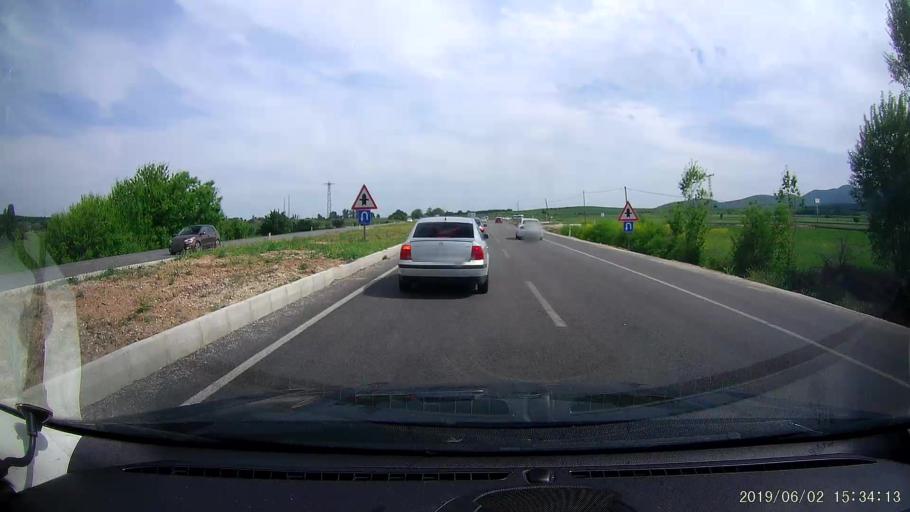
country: TR
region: Amasya
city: Saraycik
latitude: 40.9140
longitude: 35.1724
